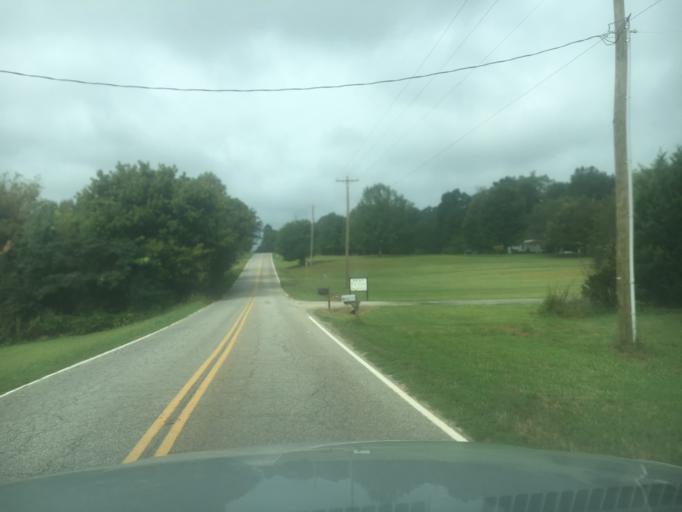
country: US
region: South Carolina
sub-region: Spartanburg County
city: Landrum
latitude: 35.1660
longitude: -82.0793
